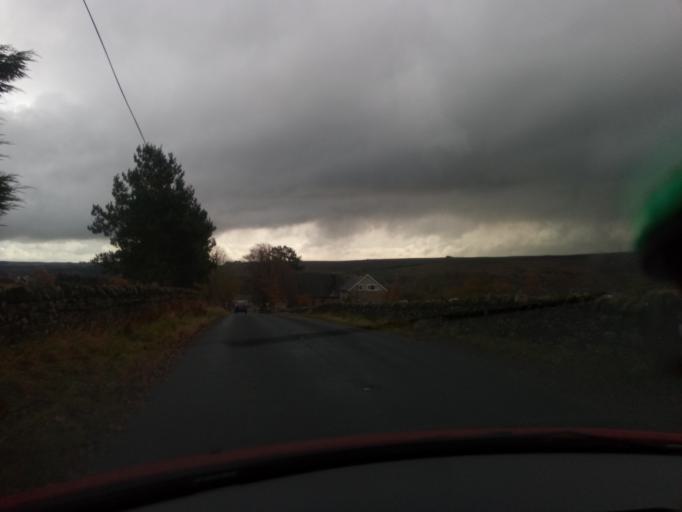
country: GB
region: England
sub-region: Northumberland
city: Corsenside
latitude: 55.1485
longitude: -2.2560
